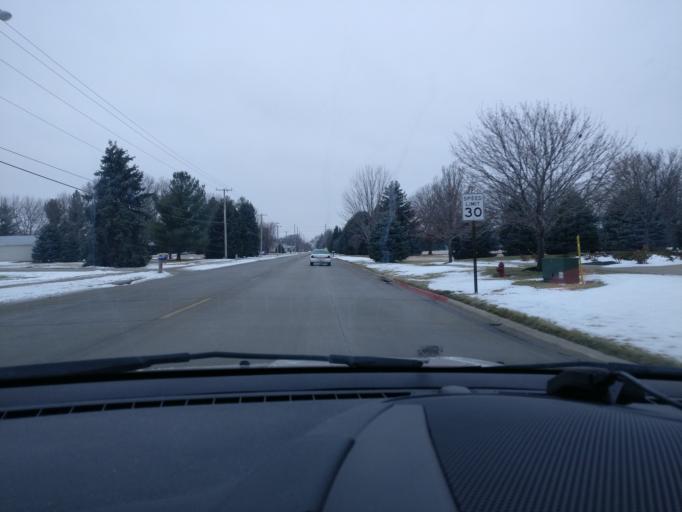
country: US
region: Nebraska
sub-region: Dodge County
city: Fremont
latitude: 41.4441
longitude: -96.4598
